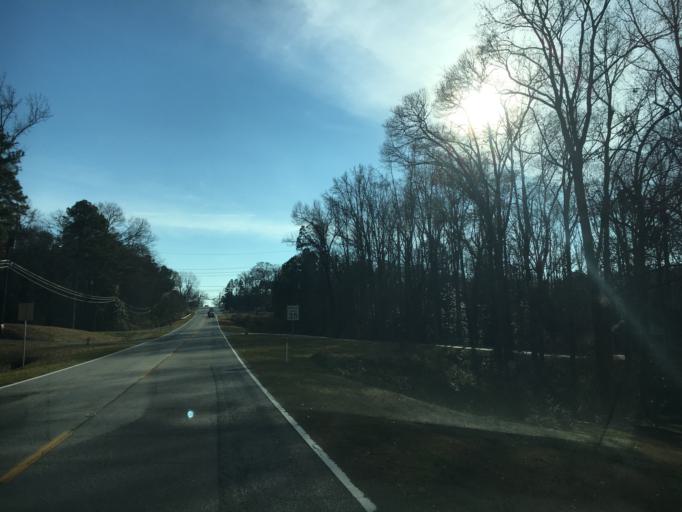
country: US
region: Georgia
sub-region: Hart County
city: Hartwell
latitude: 34.3587
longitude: -82.9350
